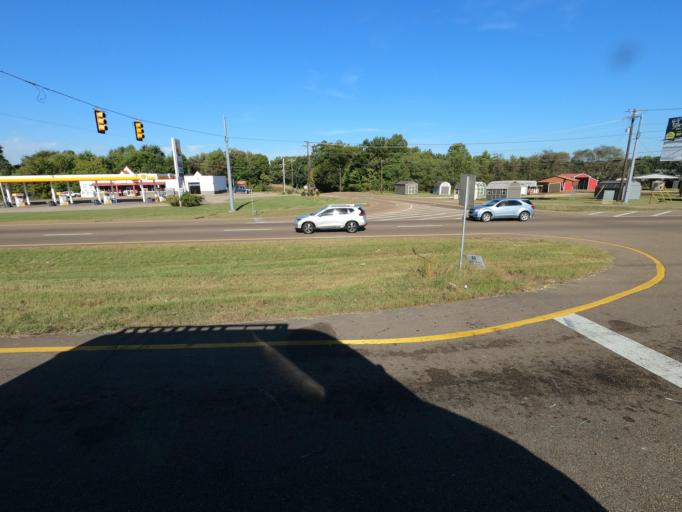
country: US
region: Tennessee
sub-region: Tipton County
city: Munford
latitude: 35.3973
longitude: -89.8487
